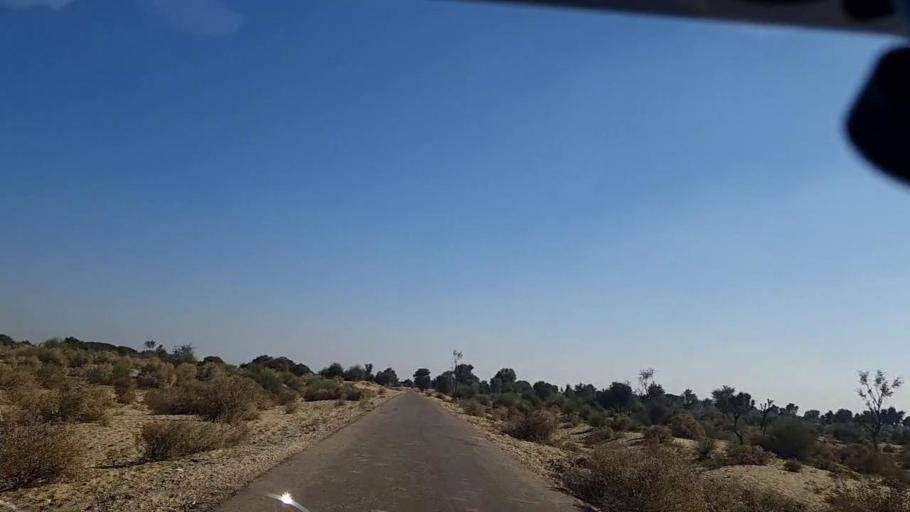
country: PK
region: Sindh
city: Khanpur
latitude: 27.6185
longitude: 69.4437
